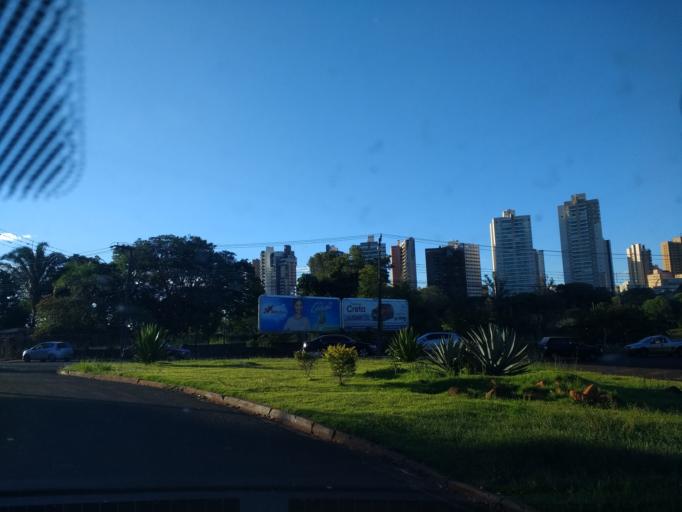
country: BR
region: Parana
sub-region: Londrina
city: Londrina
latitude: -23.3394
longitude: -51.1533
